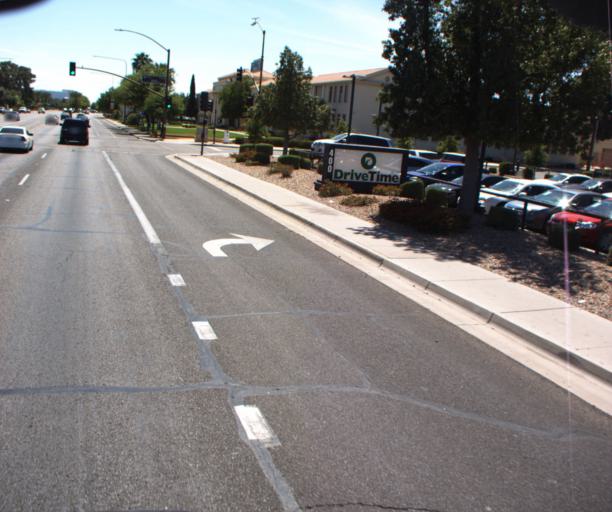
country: US
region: Arizona
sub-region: Maricopa County
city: Chandler
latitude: 33.3103
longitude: -111.8415
